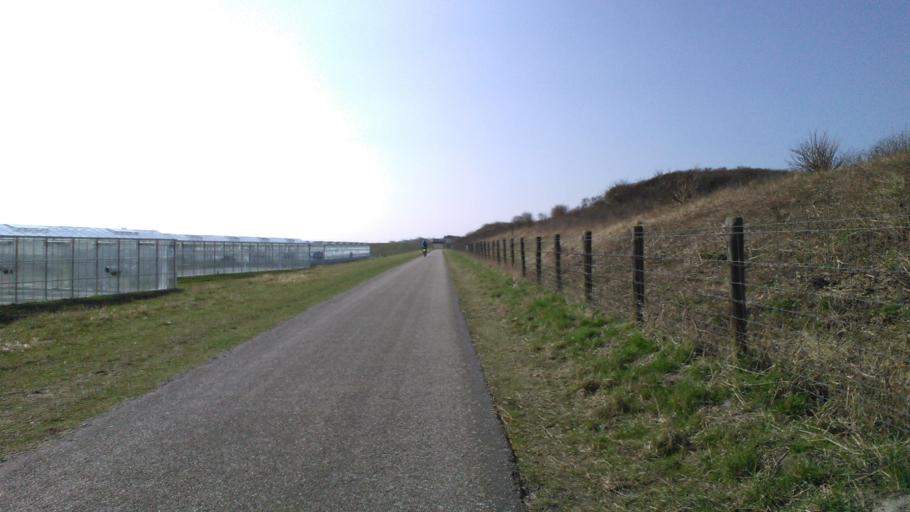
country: NL
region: South Holland
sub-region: Gemeente Westland
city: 's-Gravenzande
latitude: 52.0187
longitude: 4.1533
